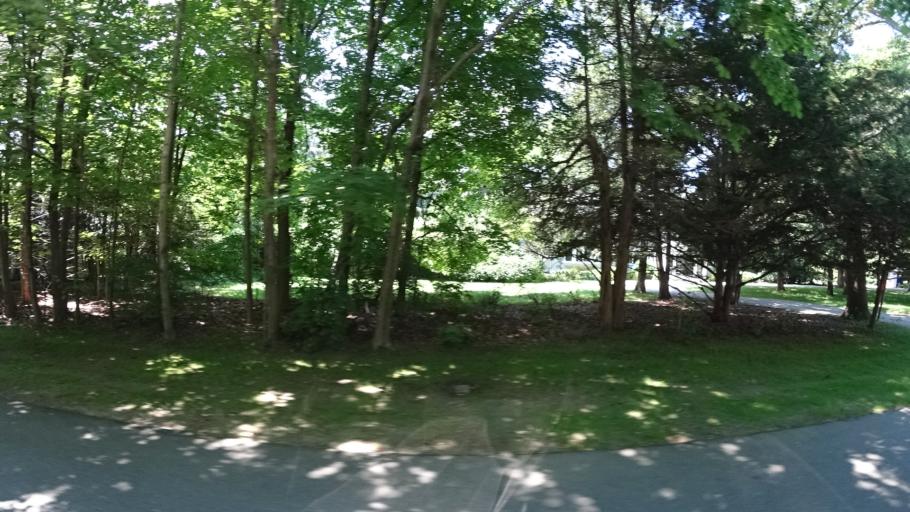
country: US
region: Massachusetts
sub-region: Norfolk County
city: Dedham
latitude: 42.2520
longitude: -71.1895
